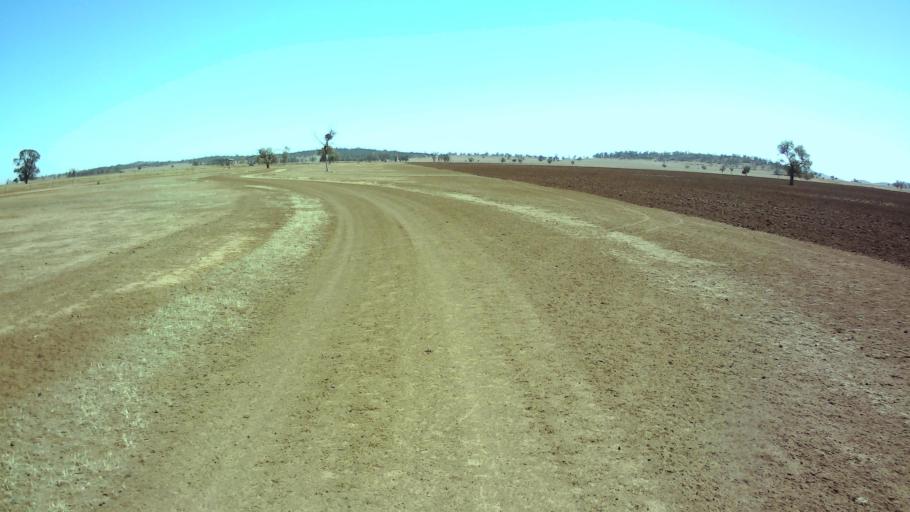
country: AU
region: New South Wales
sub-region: Forbes
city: Forbes
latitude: -33.7098
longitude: 147.6678
